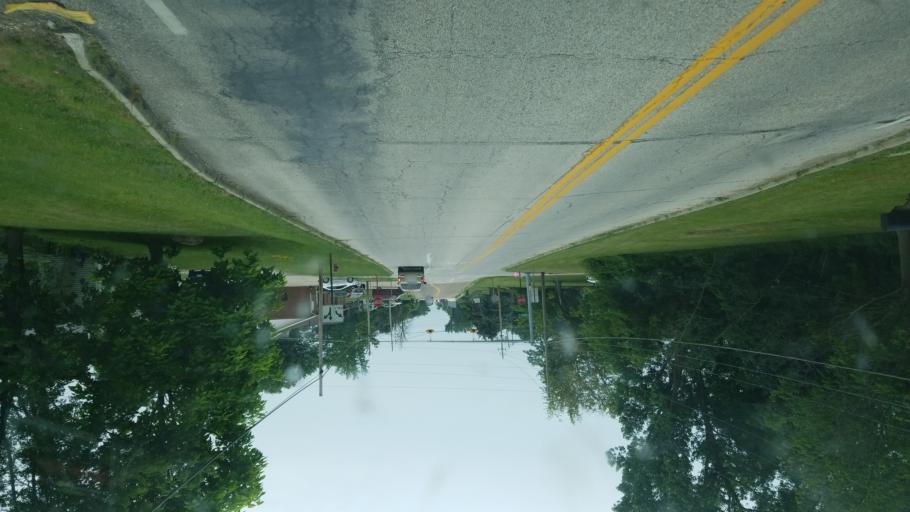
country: US
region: Ohio
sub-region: Summit County
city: Mogadore
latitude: 41.0732
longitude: -81.4172
